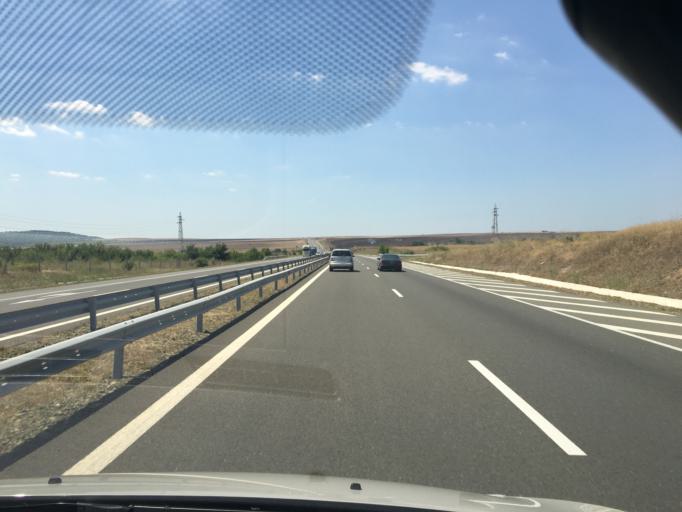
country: BG
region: Burgas
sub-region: Obshtina Karnobat
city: Karnobat
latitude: 42.5905
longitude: 26.9819
